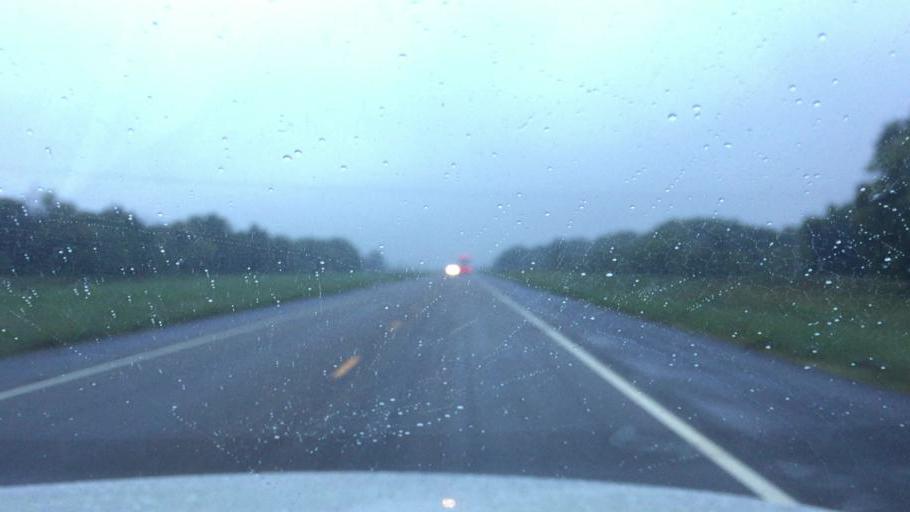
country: US
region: Kansas
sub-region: Montgomery County
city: Cherryvale
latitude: 37.4137
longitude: -95.4980
